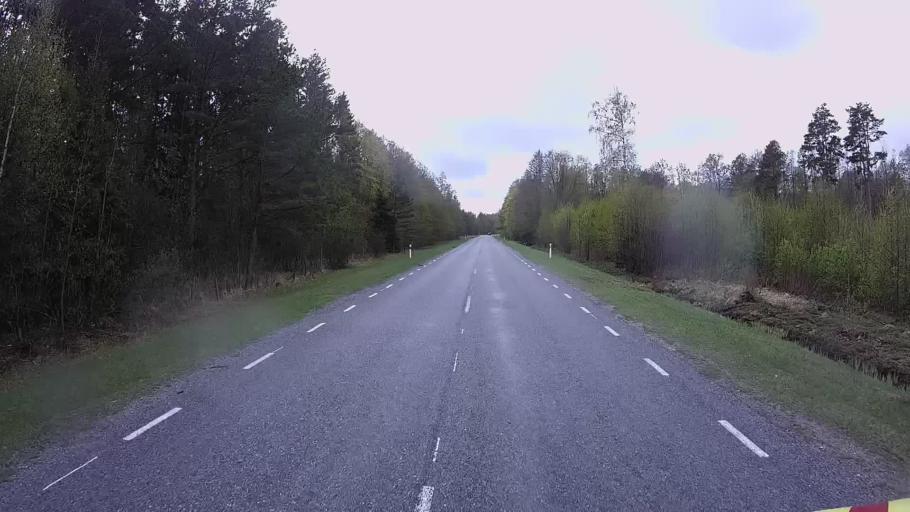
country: EE
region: Hiiumaa
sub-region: Kaerdla linn
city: Kardla
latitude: 58.7935
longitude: 22.7155
